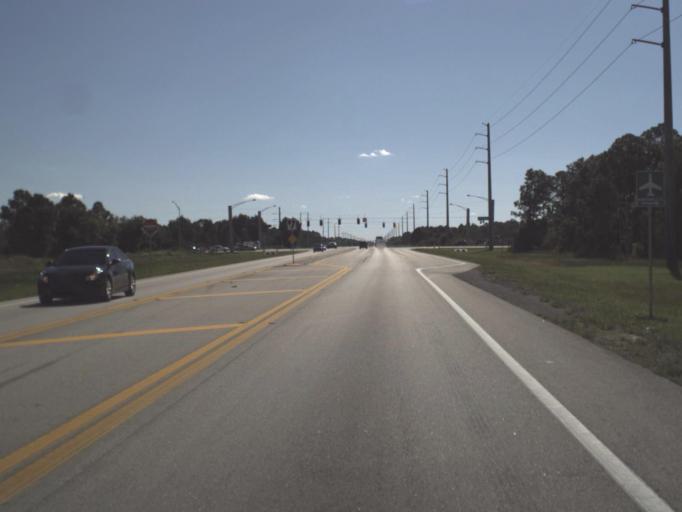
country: US
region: Florida
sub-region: Lee County
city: Gateway
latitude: 26.5828
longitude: -81.7161
